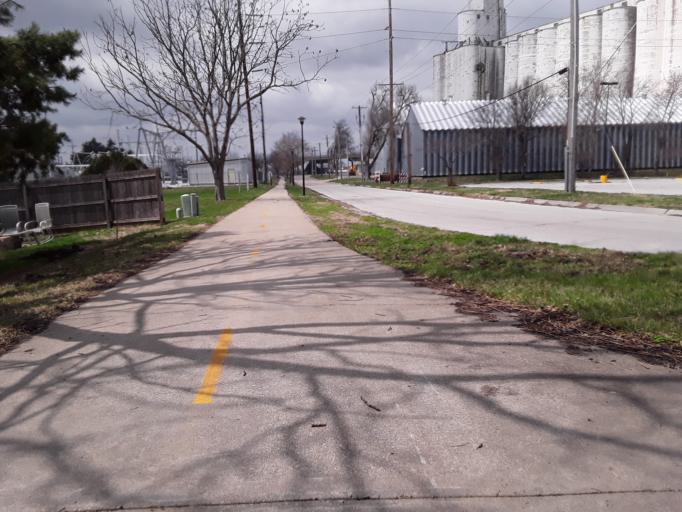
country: US
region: Nebraska
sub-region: Lancaster County
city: Lincoln
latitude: 40.8352
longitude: -96.6786
